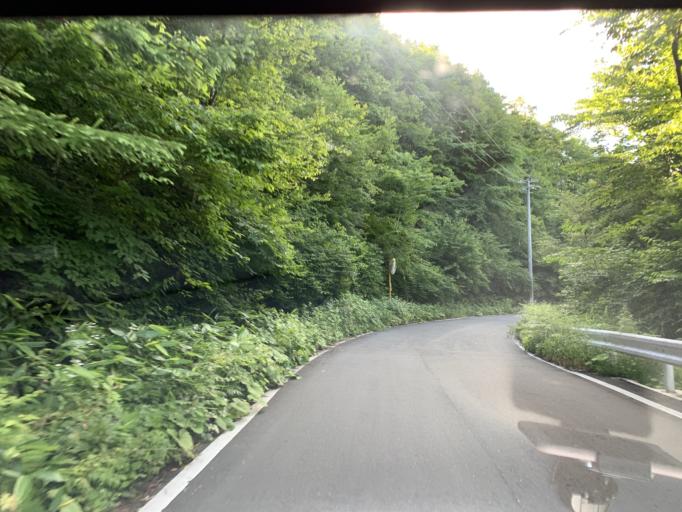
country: JP
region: Iwate
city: Ichinoseki
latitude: 38.9016
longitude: 140.8738
